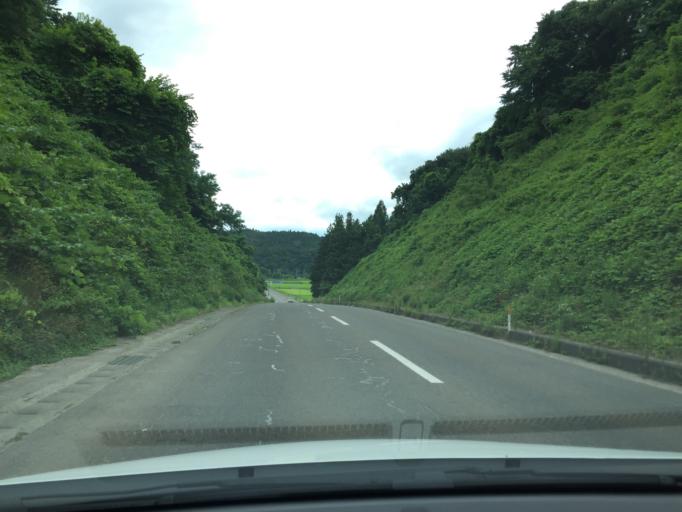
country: JP
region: Fukushima
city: Sukagawa
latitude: 37.2963
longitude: 140.2089
